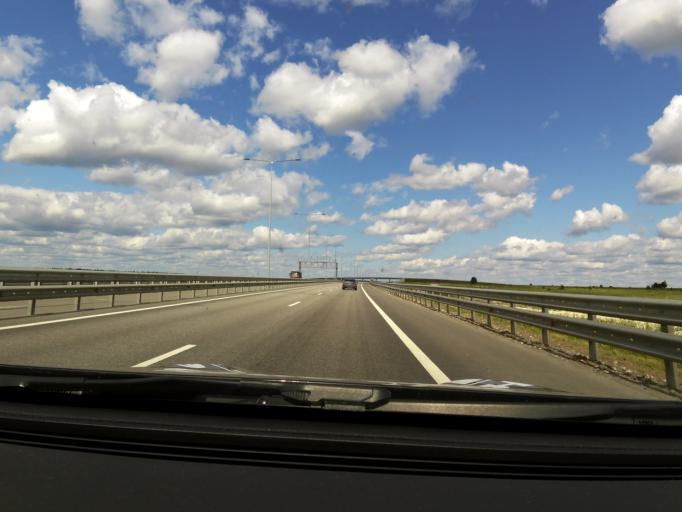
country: RU
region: Tverskaya
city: Vydropuzhsk
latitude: 57.2383
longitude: 34.9006
